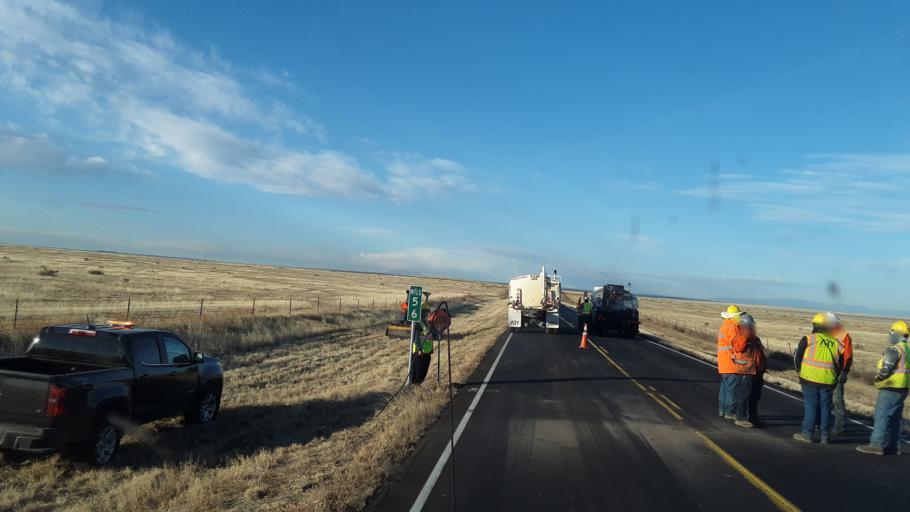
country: US
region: Colorado
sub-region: Otero County
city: Rocky Ford
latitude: 37.9628
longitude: -103.8422
